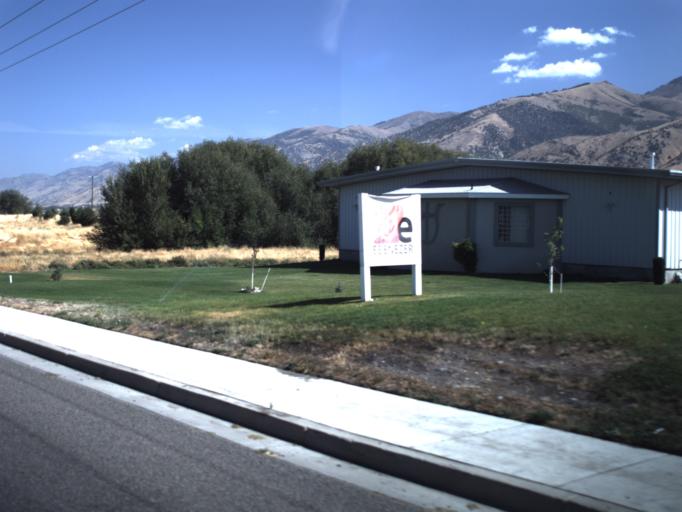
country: US
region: Utah
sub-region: Cache County
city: Hyrum
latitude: 41.6397
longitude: -111.8326
